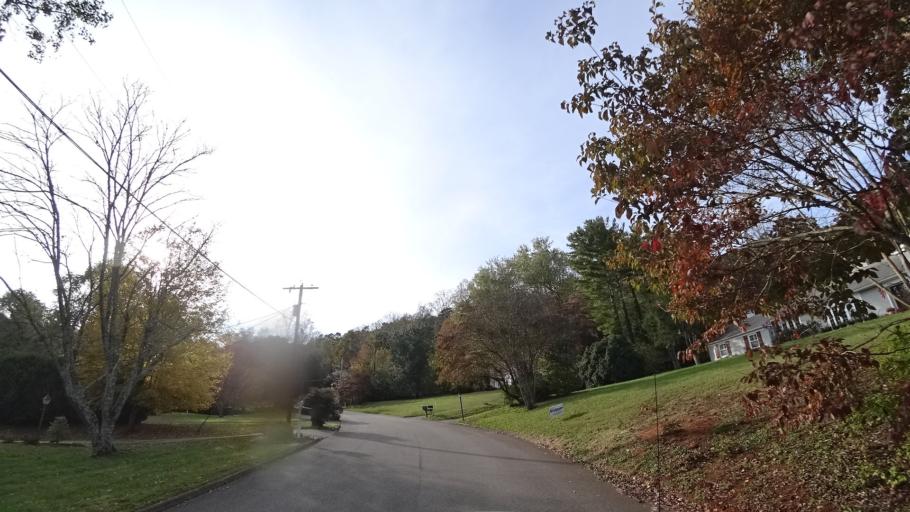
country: US
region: Tennessee
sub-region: Knox County
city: Knoxville
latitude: 35.9113
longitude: -83.9895
